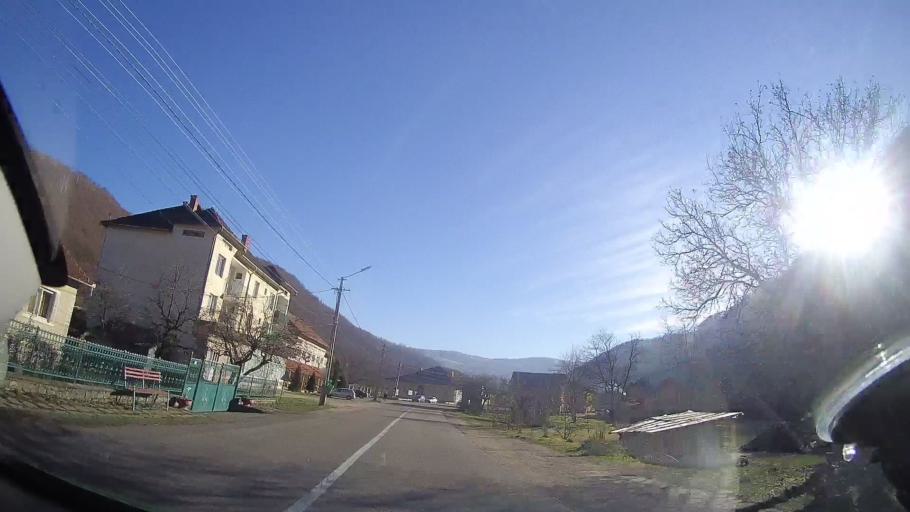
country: RO
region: Bihor
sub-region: Comuna Bulz
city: Bulz
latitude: 46.9134
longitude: 22.6747
